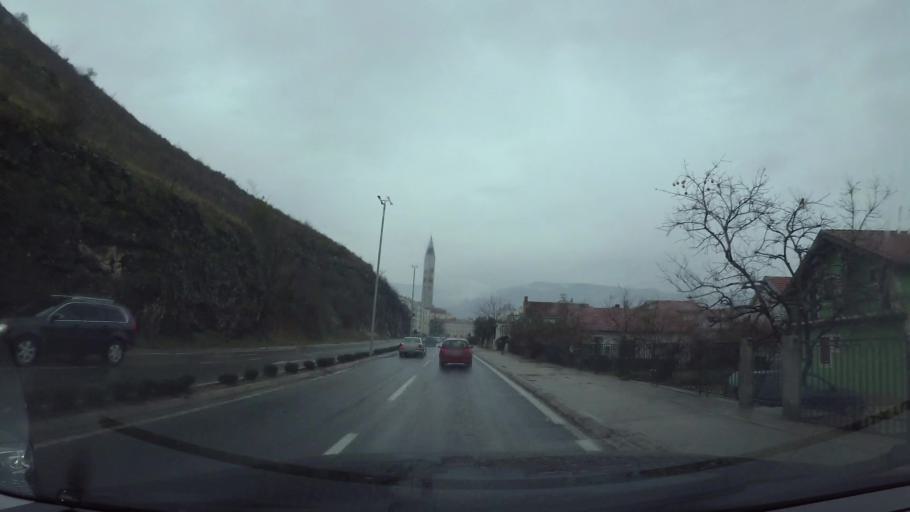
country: BA
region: Federation of Bosnia and Herzegovina
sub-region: Hercegovacko-Bosanski Kanton
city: Mostar
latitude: 43.3356
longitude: 17.8125
